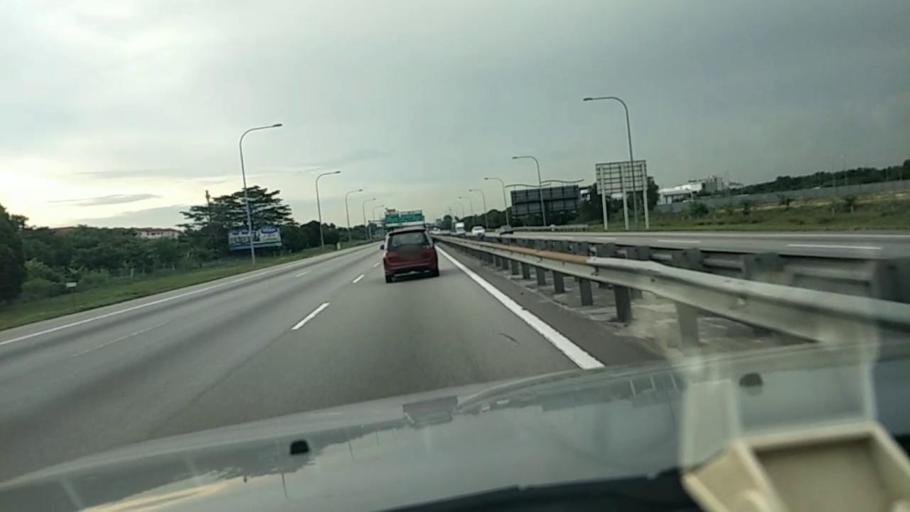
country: MY
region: Selangor
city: Subang Jaya
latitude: 2.9538
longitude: 101.5862
